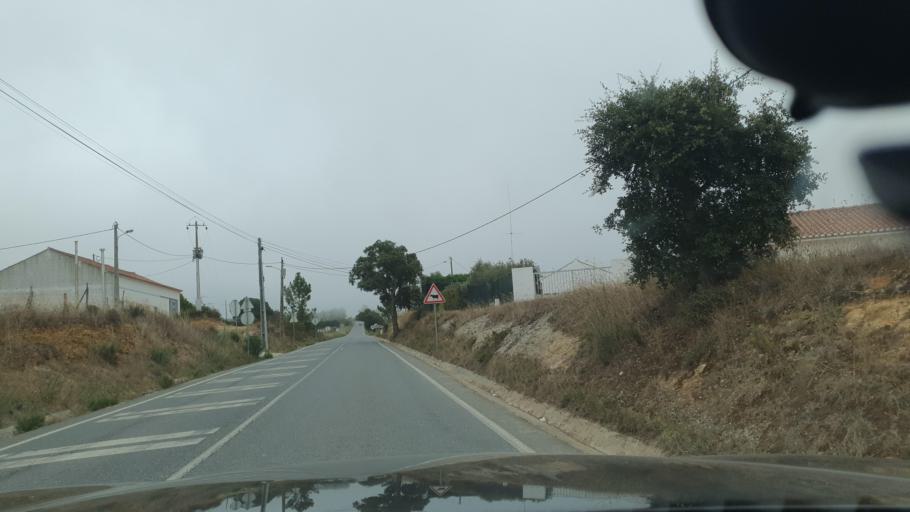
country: PT
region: Beja
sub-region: Odemira
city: Sao Teotonio
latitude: 37.5318
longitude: -8.7170
